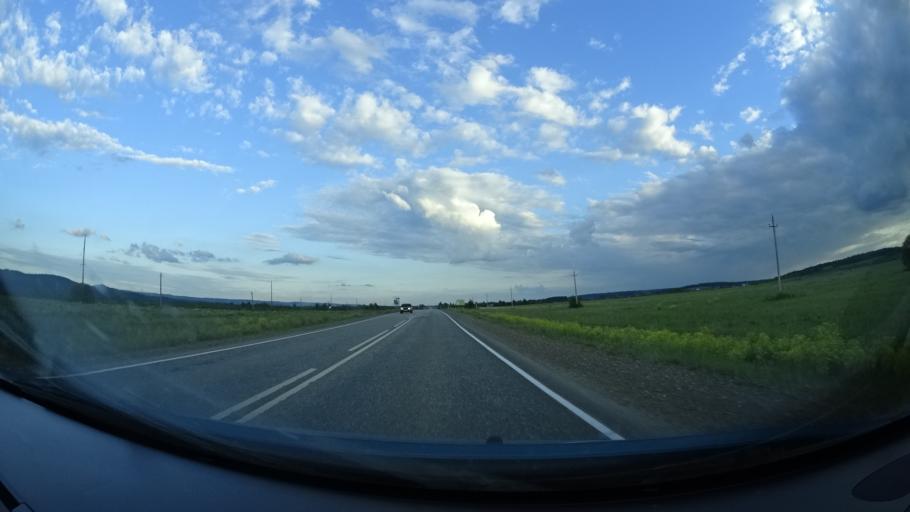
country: RU
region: Perm
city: Barda
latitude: 56.9789
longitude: 55.5768
